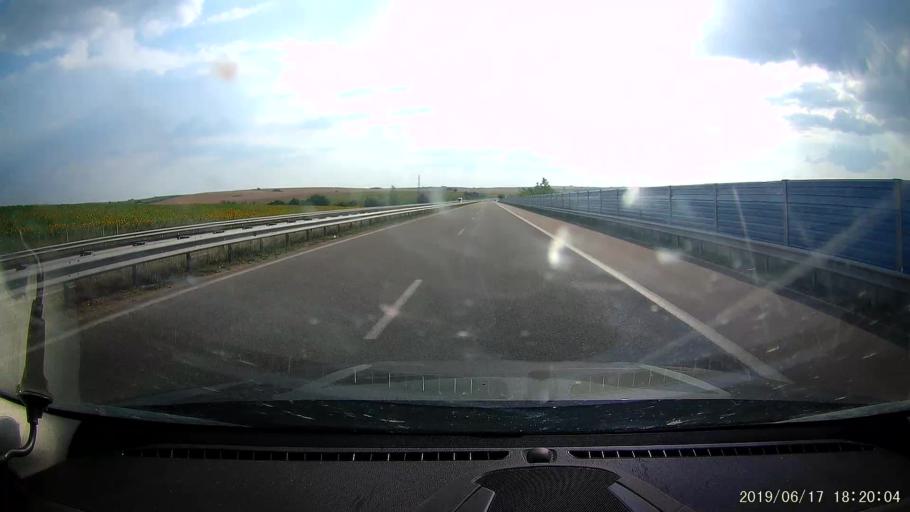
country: BG
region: Khaskovo
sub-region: Obshtina Simeonovgrad
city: Simeonovgrad
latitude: 41.9625
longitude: 25.8258
